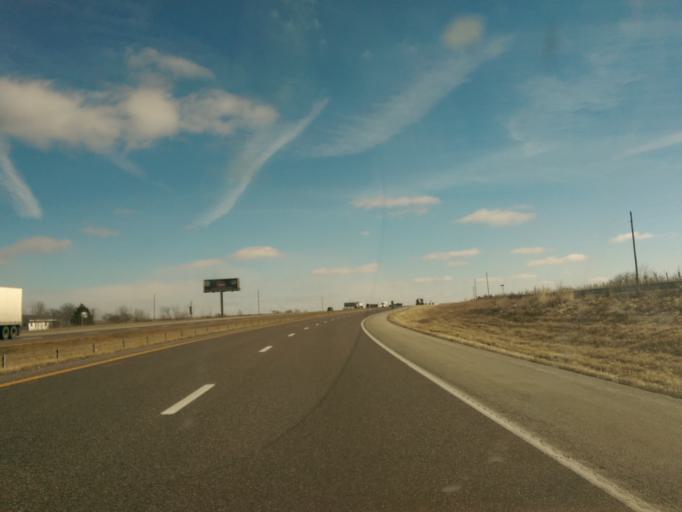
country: US
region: Missouri
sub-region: Callaway County
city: Fulton
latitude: 38.9434
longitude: -91.8804
